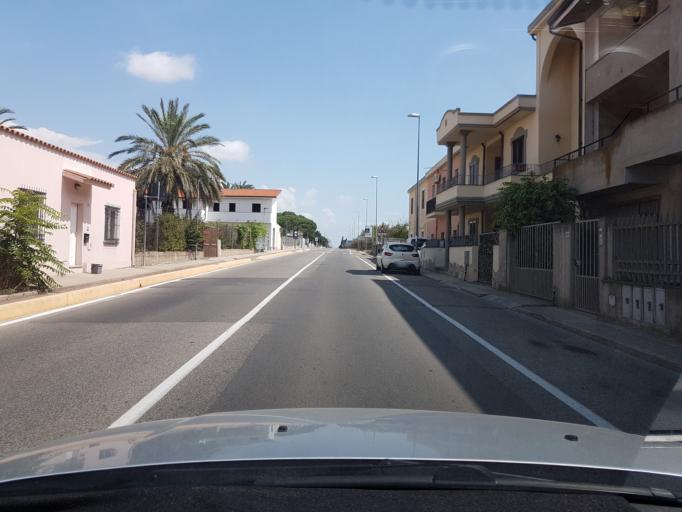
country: IT
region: Sardinia
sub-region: Provincia di Oristano
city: Oristano
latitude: 39.9096
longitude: 8.6036
